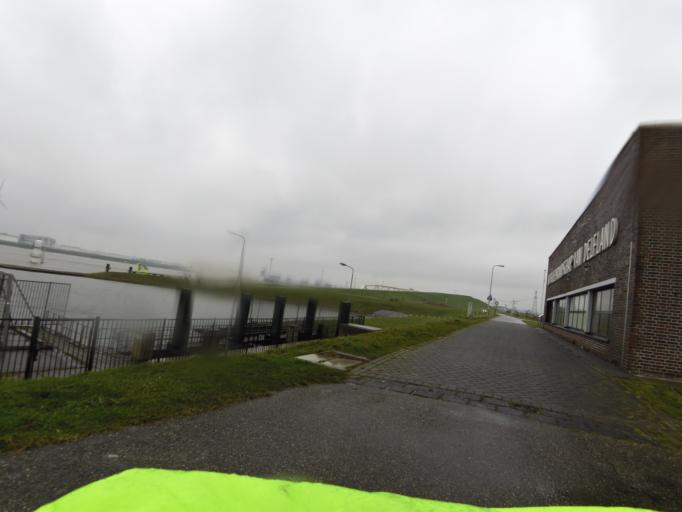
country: NL
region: South Holland
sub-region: Gemeente Westland
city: Maasdijk
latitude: 51.9541
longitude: 4.1740
